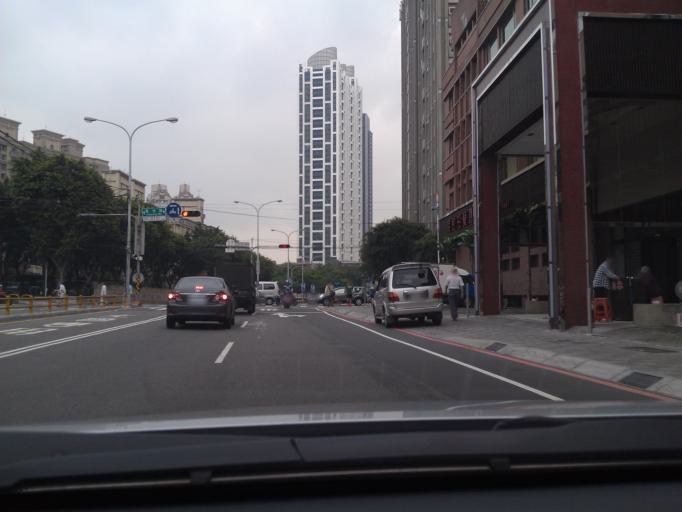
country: TW
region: Taipei
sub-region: Taipei
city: Banqiao
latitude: 25.0237
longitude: 121.4747
